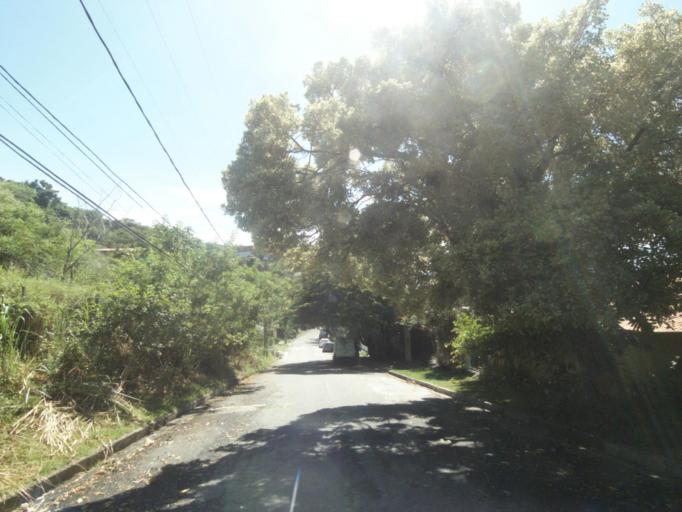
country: BR
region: Rio de Janeiro
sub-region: Niteroi
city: Niteroi
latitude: -22.9572
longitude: -43.0675
